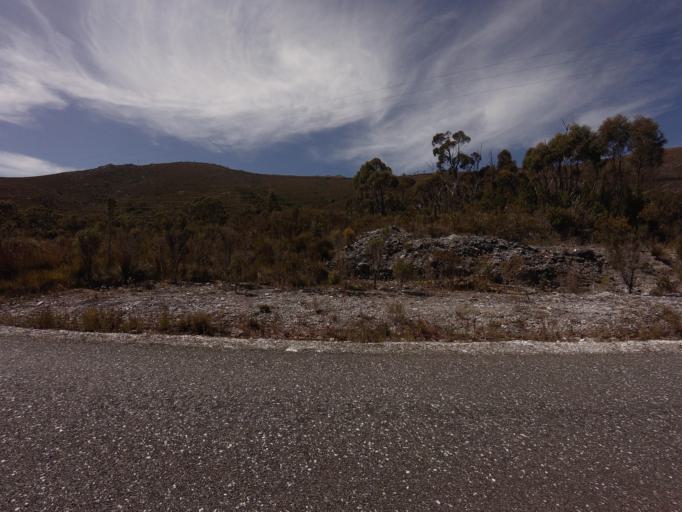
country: AU
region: Tasmania
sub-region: West Coast
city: Queenstown
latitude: -42.7850
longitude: 146.0618
